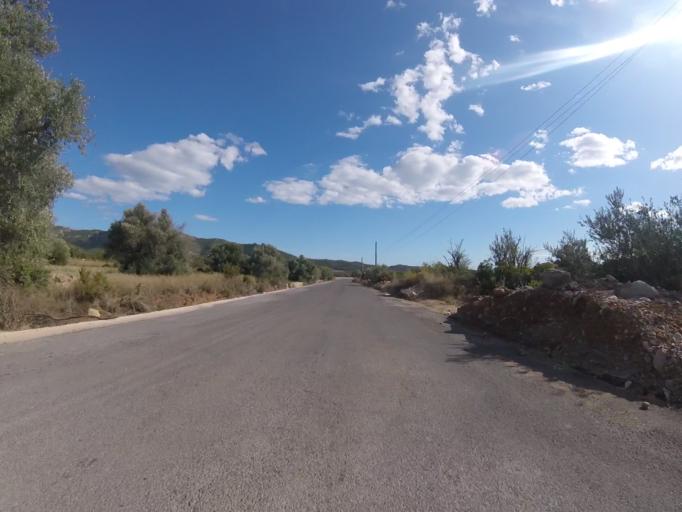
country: ES
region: Valencia
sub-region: Provincia de Castello
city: Alcala de Xivert
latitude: 40.2705
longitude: 0.2393
